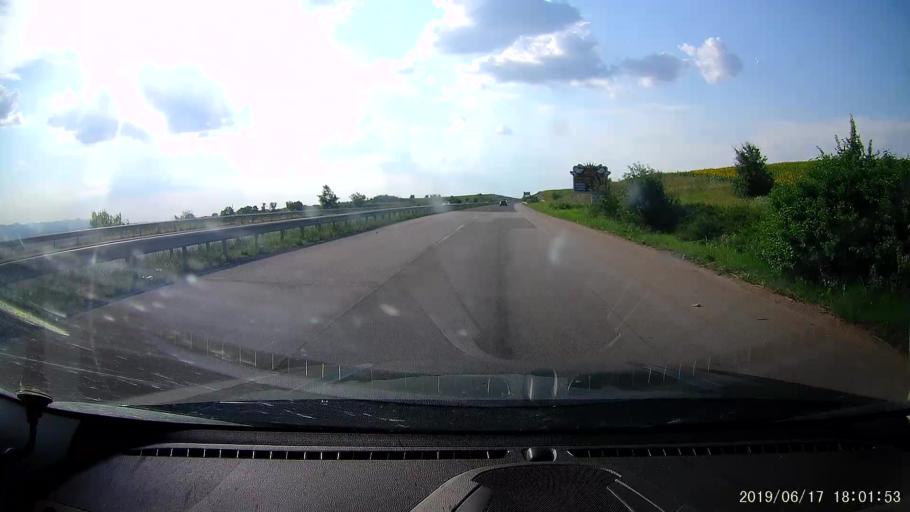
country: BG
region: Khaskovo
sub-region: Obshtina Svilengrad
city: Svilengrad
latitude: 41.7500
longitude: 26.2421
